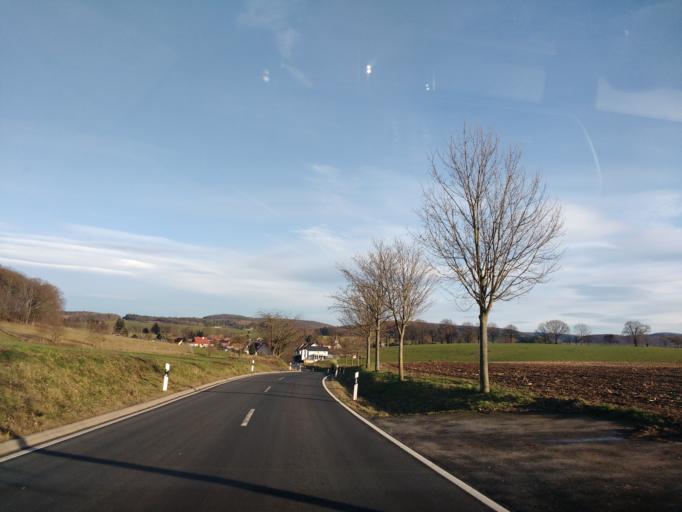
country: DE
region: Thuringia
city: Burgwalde
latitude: 51.3883
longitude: 10.0352
